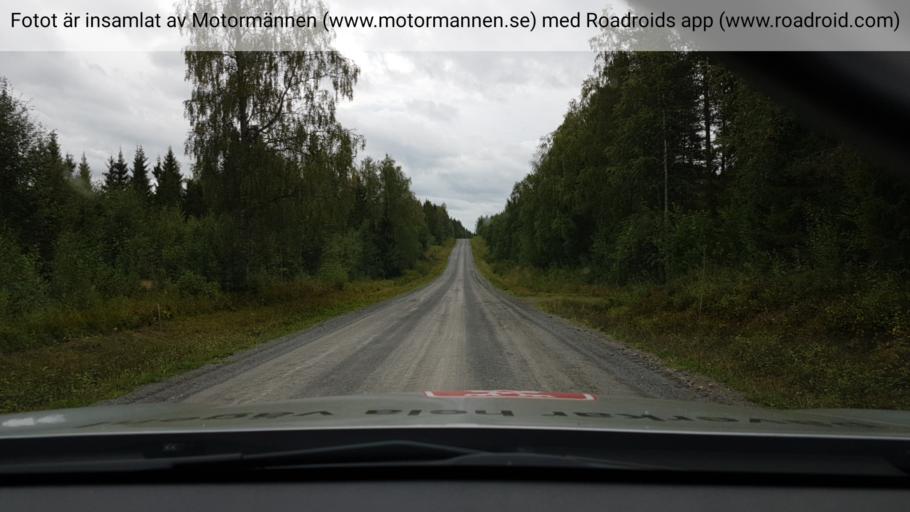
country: SE
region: Vaesterbotten
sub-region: Skelleftea Kommun
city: Forsbacka
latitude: 64.7814
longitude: 20.5143
